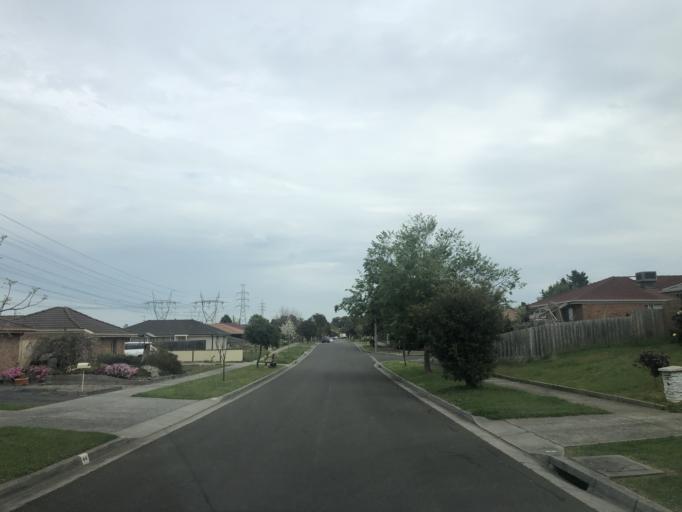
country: AU
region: Victoria
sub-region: Casey
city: Hallam
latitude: -38.0059
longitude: 145.2833
